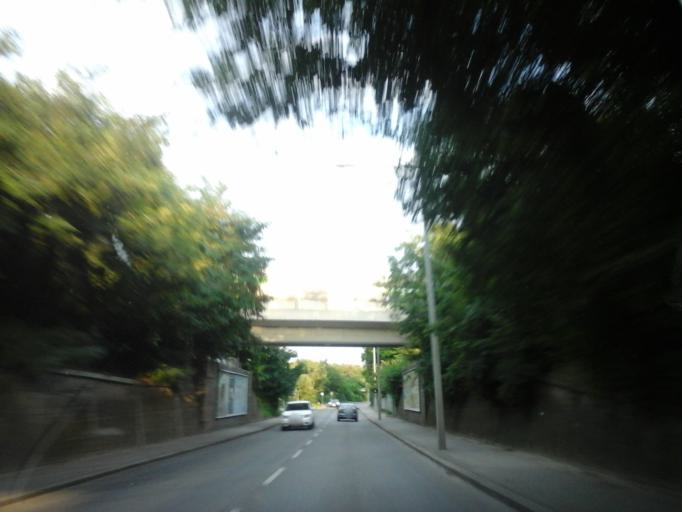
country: AT
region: Lower Austria
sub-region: Politischer Bezirk Wien-Umgebung
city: Schwechat
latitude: 48.1698
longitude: 16.4784
